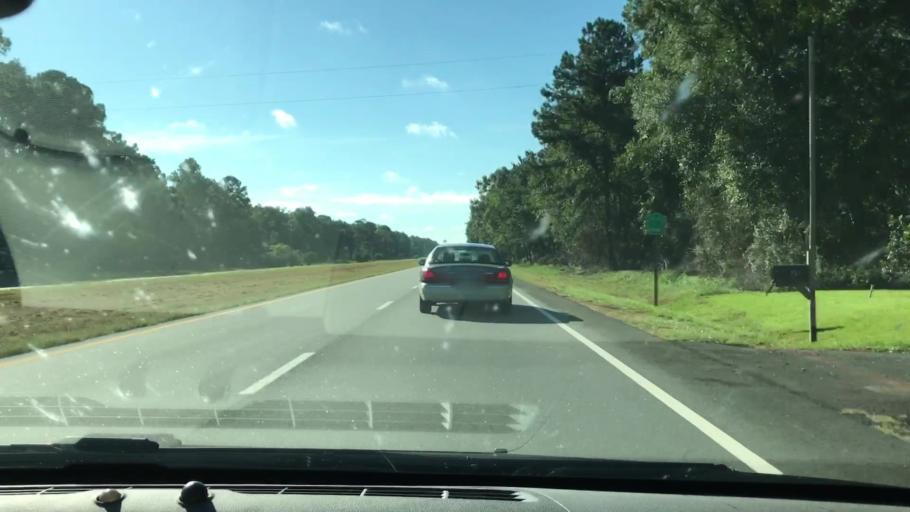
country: US
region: Georgia
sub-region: Lee County
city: Leesburg
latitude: 31.6600
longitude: -84.2756
